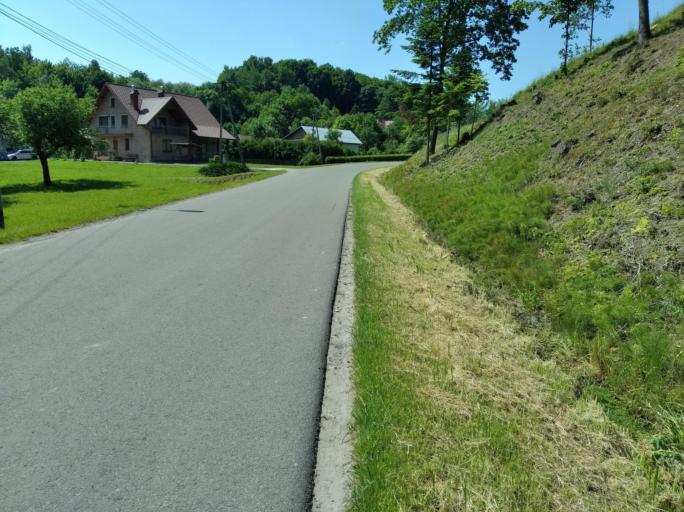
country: PL
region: Subcarpathian Voivodeship
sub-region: Powiat ropczycko-sedziszowski
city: Zagorzyce
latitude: 49.9988
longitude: 21.6529
